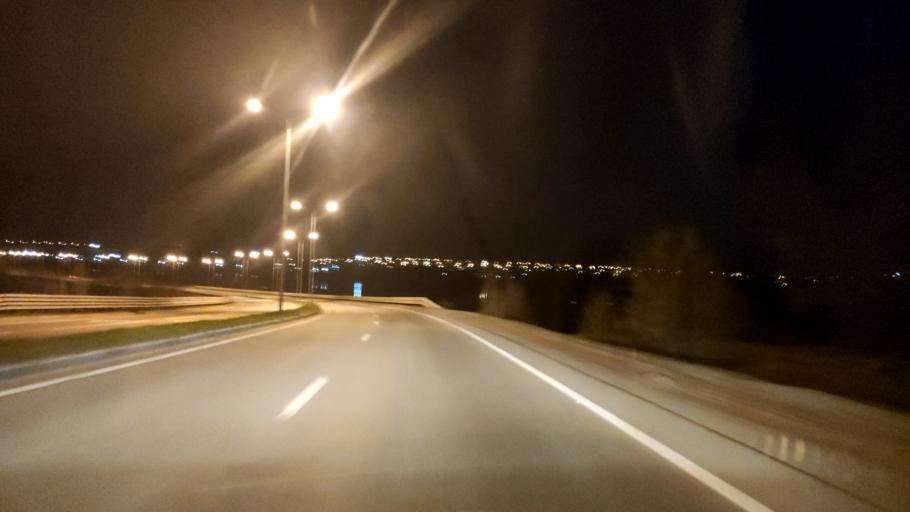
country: RU
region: Belgorod
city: Staryy Oskol
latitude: 51.2855
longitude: 37.7882
